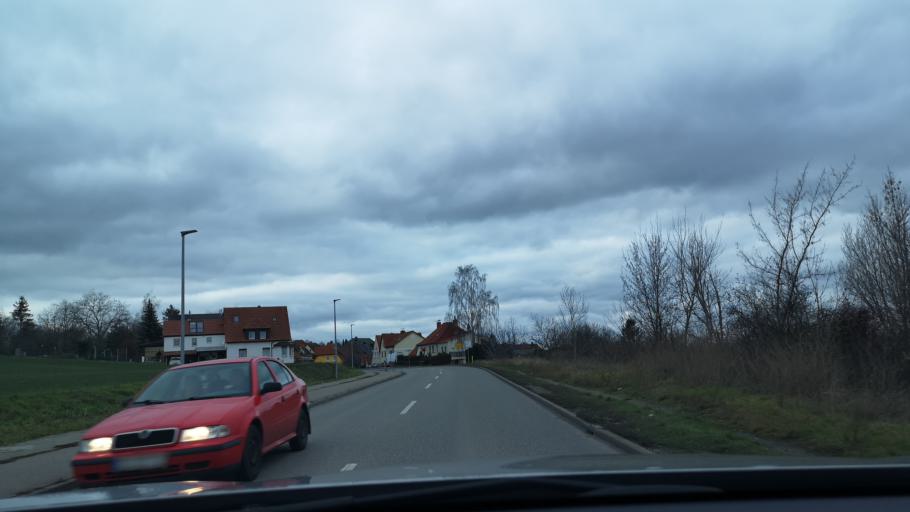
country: DE
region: Saxony-Anhalt
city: Krumpa
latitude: 51.2992
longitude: 11.8379
